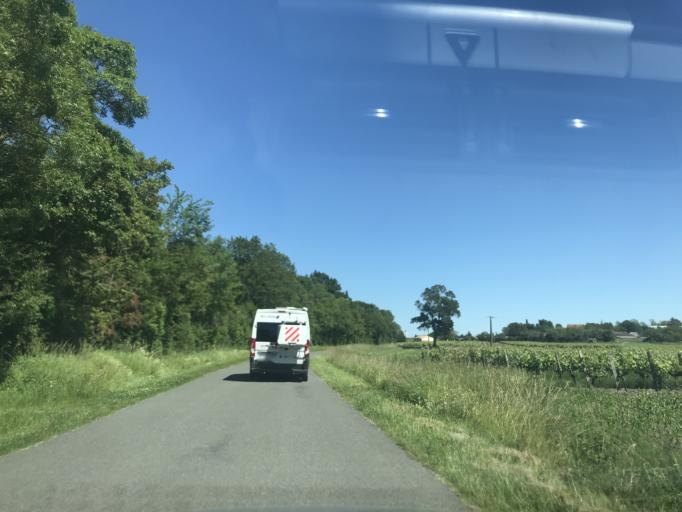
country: FR
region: Poitou-Charentes
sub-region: Departement de la Charente-Maritime
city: Mortagne-sur-Gironde
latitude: 45.4232
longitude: -0.7180
